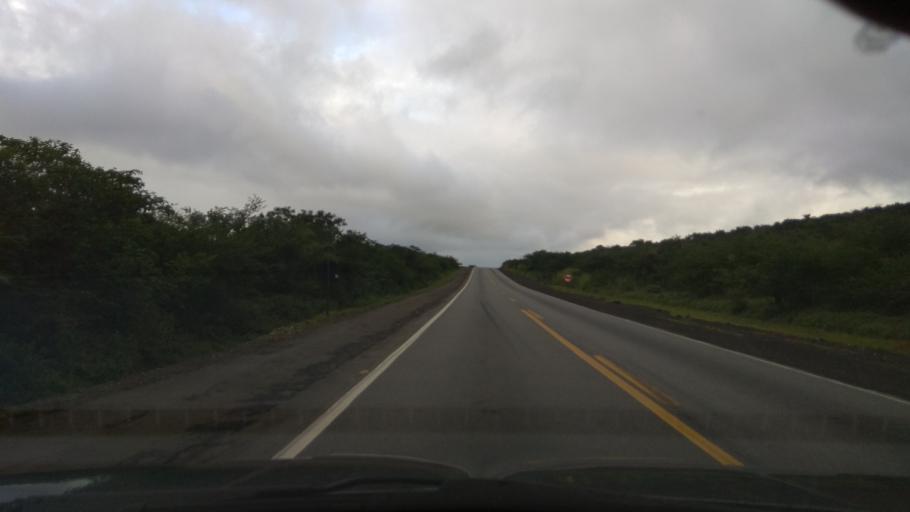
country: BR
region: Bahia
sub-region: Jaguaquara
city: Jaguaquara
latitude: -13.3487
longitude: -40.0165
